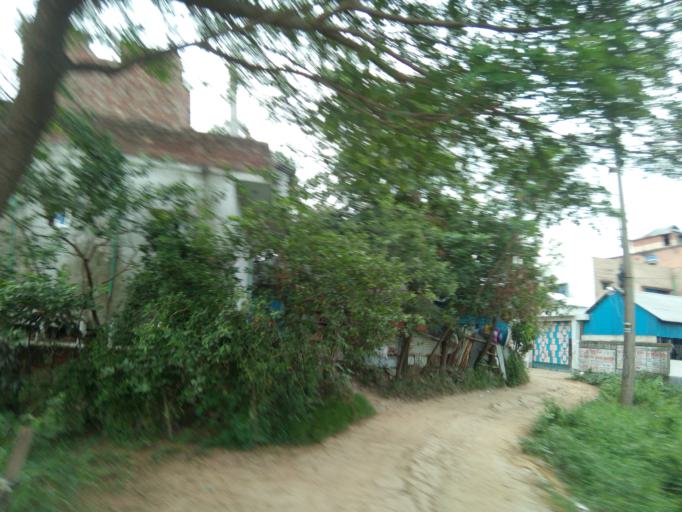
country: BD
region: Dhaka
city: Paltan
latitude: 23.7392
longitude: 90.4601
